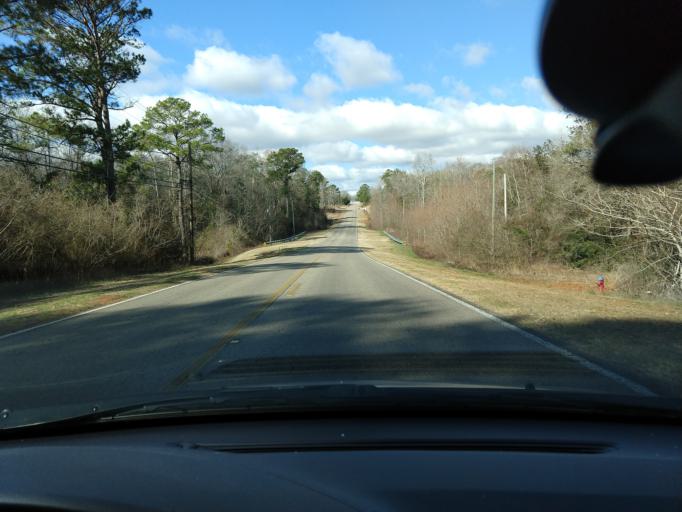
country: US
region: Alabama
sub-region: Coffee County
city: Enterprise
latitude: 31.3218
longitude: -85.8774
